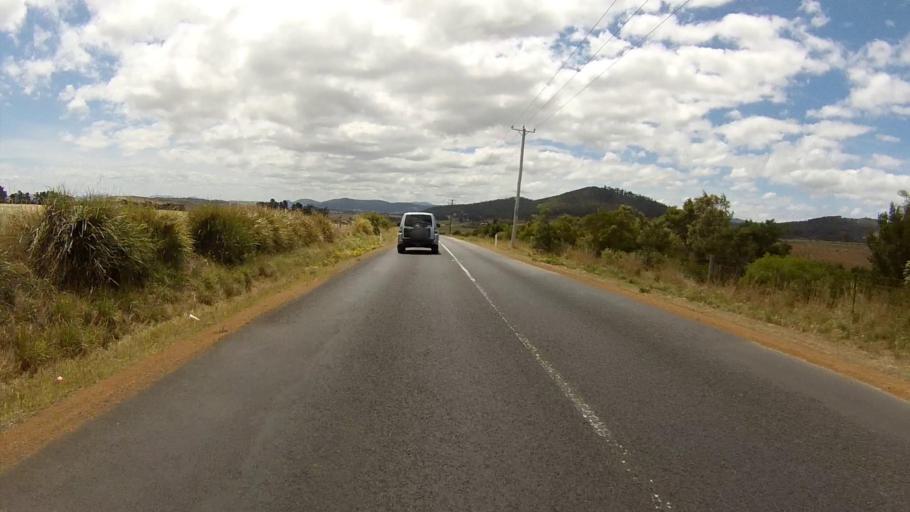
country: AU
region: Tasmania
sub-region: Sorell
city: Sorell
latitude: -42.8130
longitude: 147.6137
